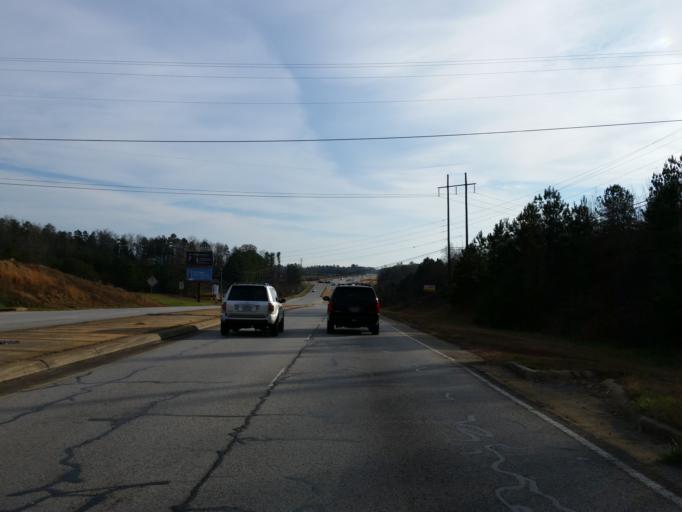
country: US
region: Georgia
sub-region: Paulding County
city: Hiram
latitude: 33.9076
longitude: -84.7790
